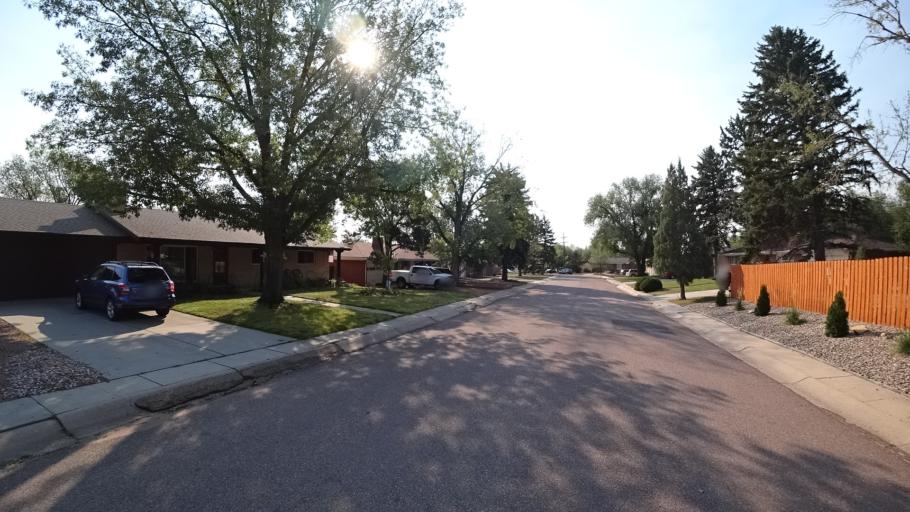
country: US
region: Colorado
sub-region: El Paso County
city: Colorado Springs
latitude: 38.8141
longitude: -104.8509
